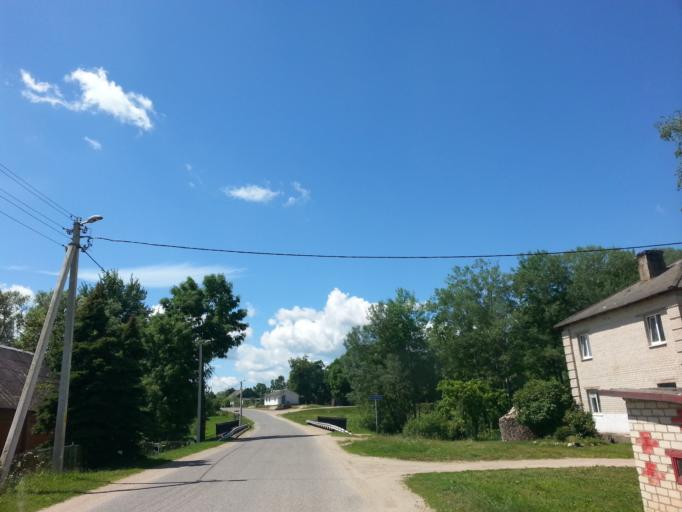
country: BY
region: Vitebsk
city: Mosar
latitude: 55.2325
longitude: 27.4754
